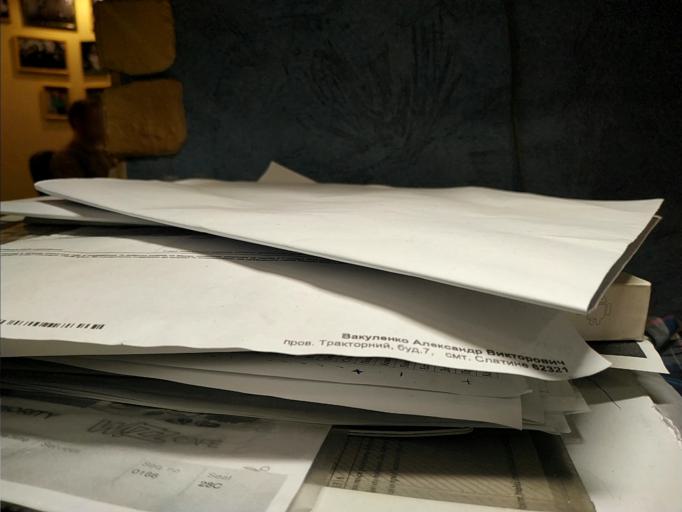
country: RU
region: Tverskaya
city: Zubtsov
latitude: 56.1167
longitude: 34.5931
